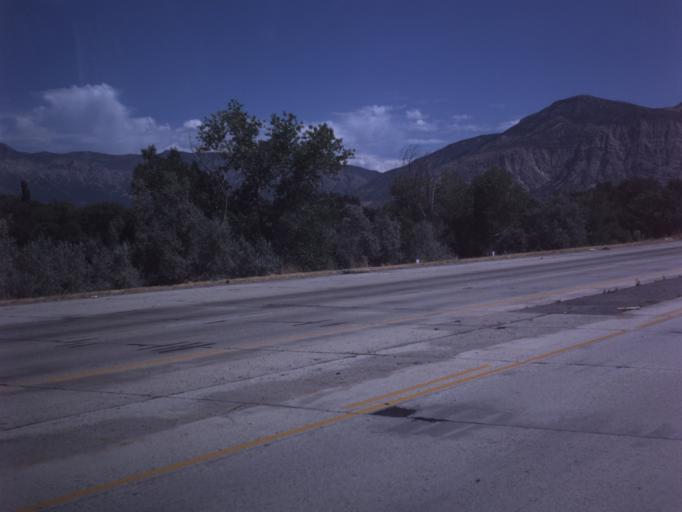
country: US
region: Utah
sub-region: Weber County
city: Ogden
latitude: 41.2307
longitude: -111.9916
